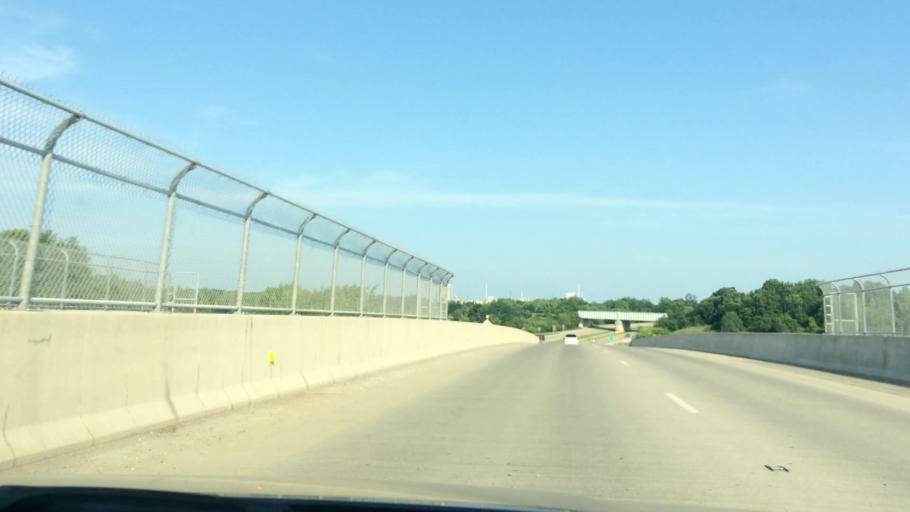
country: US
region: Indiana
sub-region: Tippecanoe County
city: Lafayette
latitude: 40.4488
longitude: -86.8777
